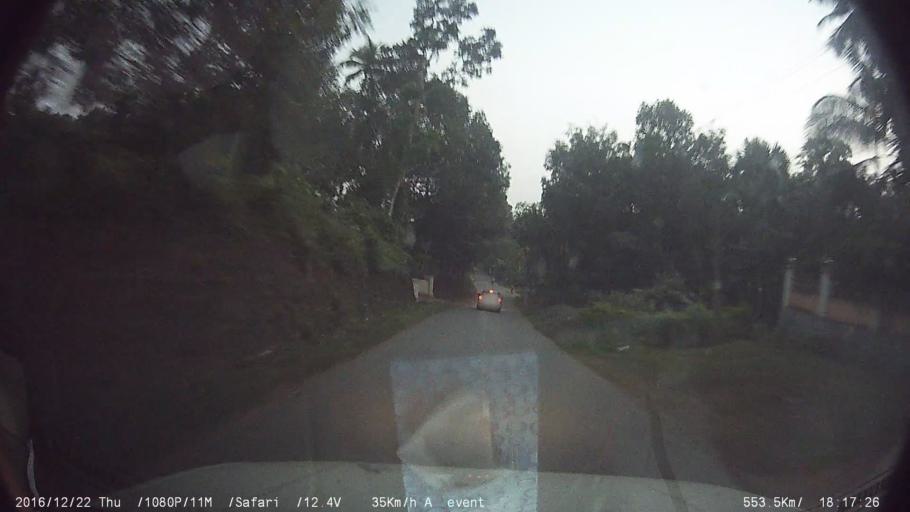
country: IN
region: Kerala
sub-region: Kottayam
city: Palackattumala
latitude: 9.7654
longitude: 76.6103
